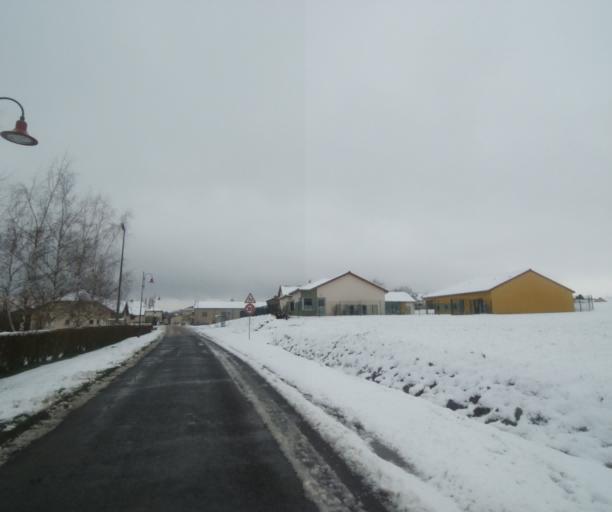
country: FR
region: Champagne-Ardenne
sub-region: Departement de la Haute-Marne
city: Laneuville-a-Remy
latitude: 48.5073
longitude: 4.8700
